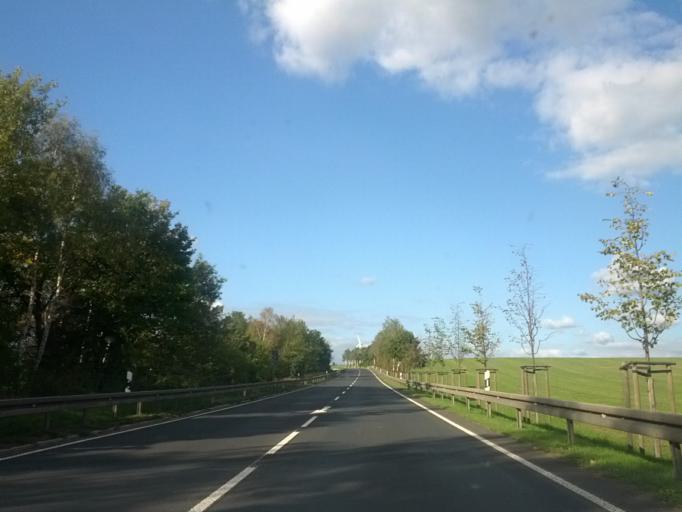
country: DE
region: Thuringia
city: Fambach
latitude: 50.7462
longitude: 10.3563
